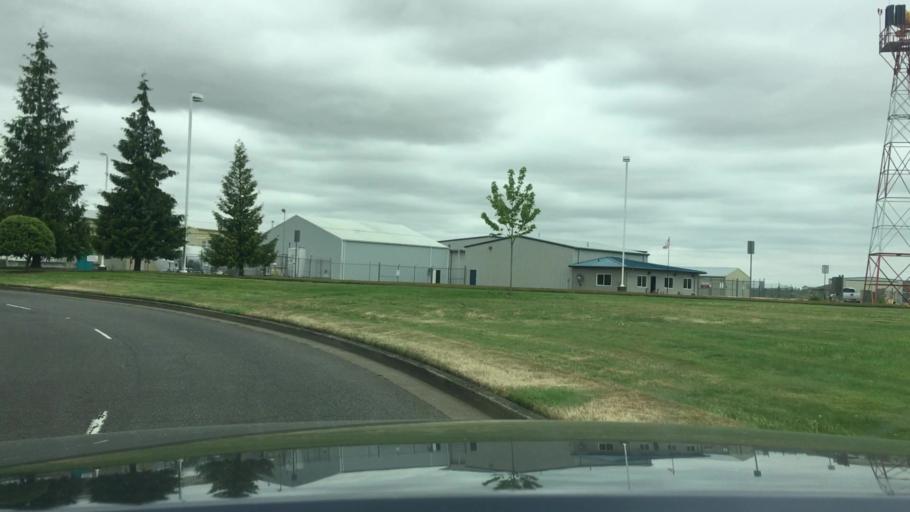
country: US
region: Oregon
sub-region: Lane County
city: Junction City
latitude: 44.1205
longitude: -123.2089
